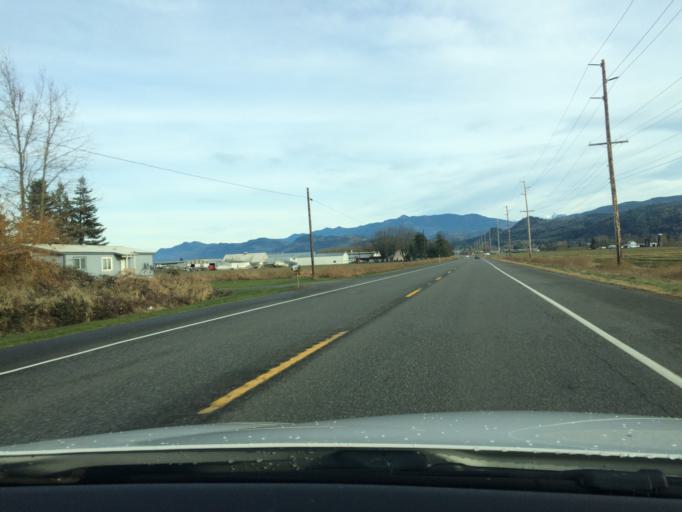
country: US
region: Washington
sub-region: Whatcom County
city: Nooksack
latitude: 48.9638
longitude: -122.3022
